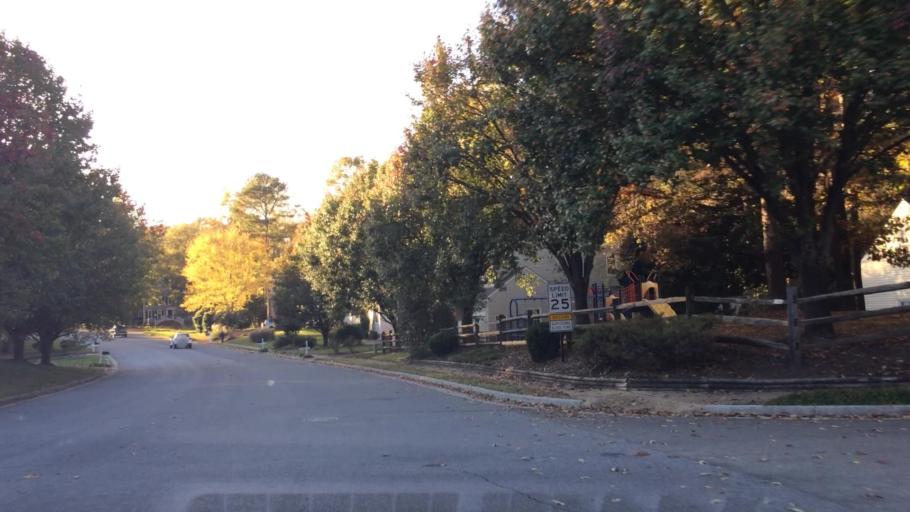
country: US
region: Virginia
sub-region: Henrico County
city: Chamberlayne
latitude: 37.6882
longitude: -77.4215
